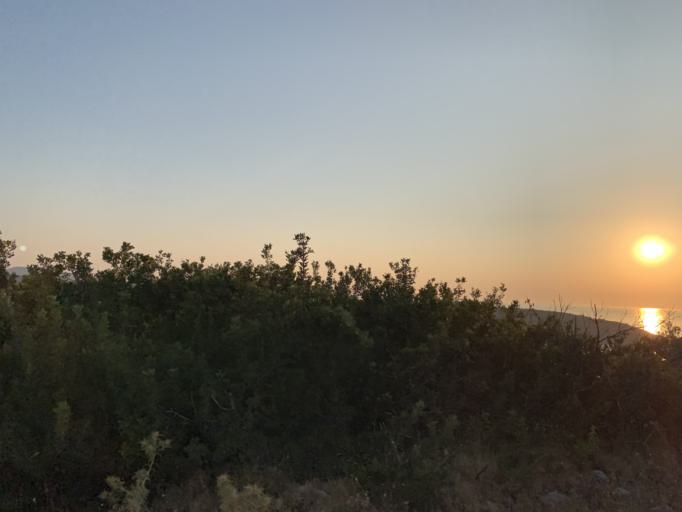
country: GR
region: North Aegean
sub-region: Chios
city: Thymiana
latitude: 38.3415
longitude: 25.9992
